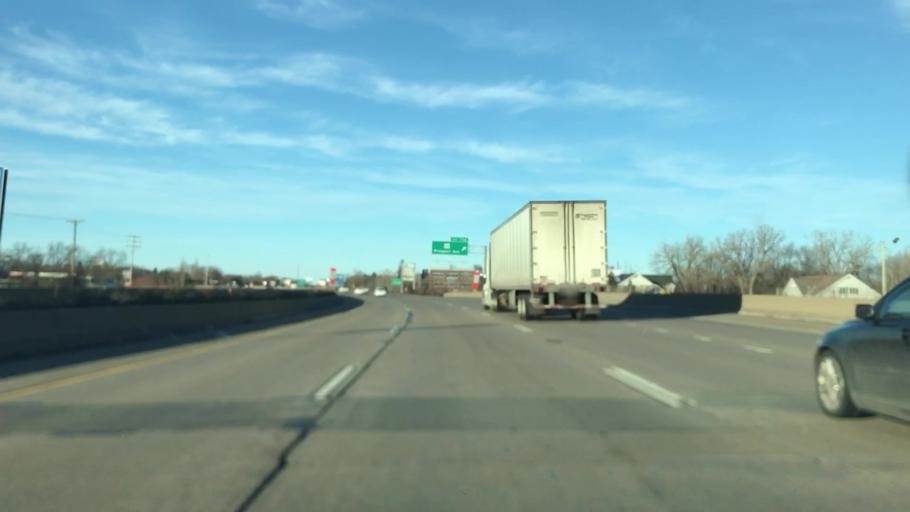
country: US
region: Wisconsin
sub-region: Winnebago County
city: Menasha
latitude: 44.2397
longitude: -88.4649
